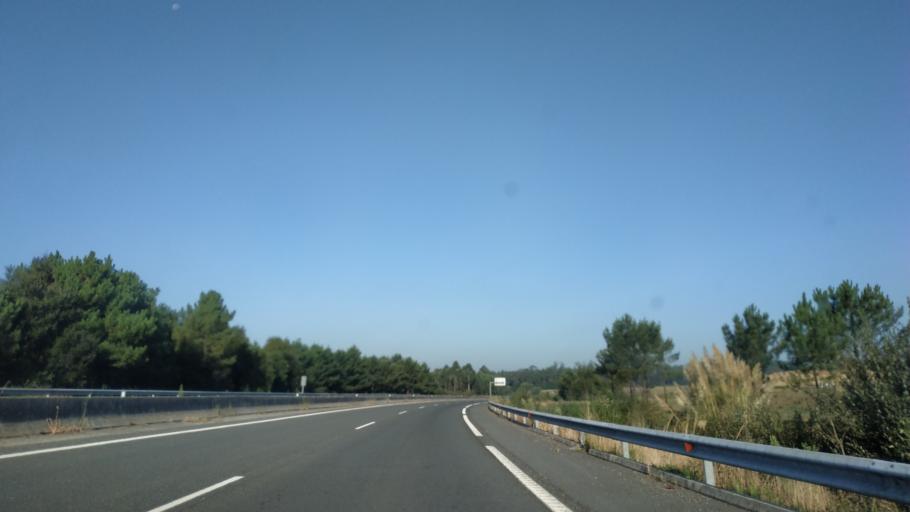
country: ES
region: Galicia
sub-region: Provincia da Coruna
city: Laracha
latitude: 43.2555
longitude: -8.6158
